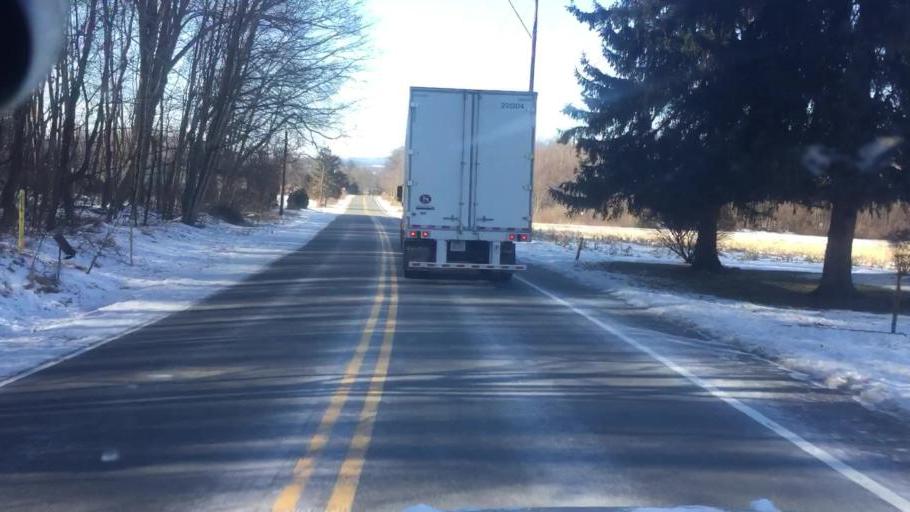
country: US
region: Pennsylvania
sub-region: Luzerne County
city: Nescopeck
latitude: 41.0546
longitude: -76.1766
